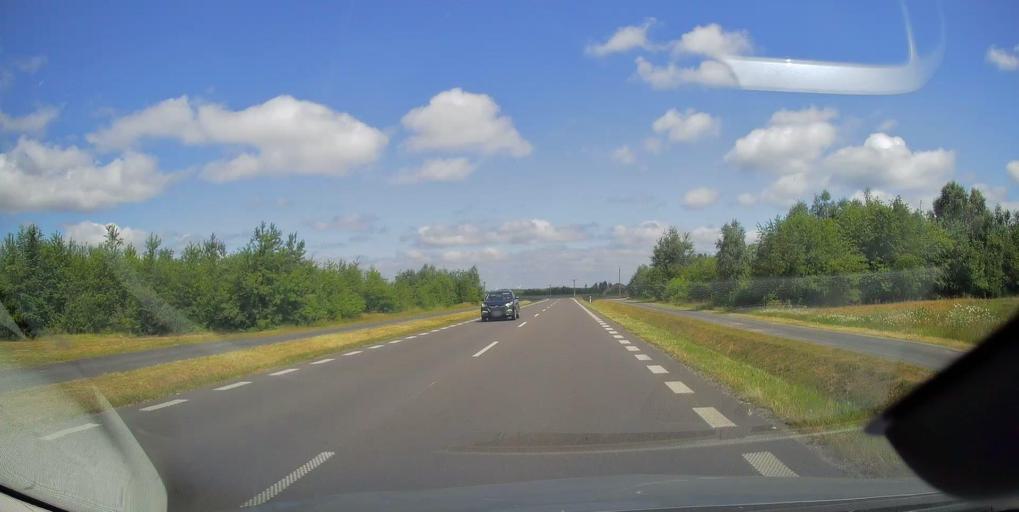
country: PL
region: Subcarpathian Voivodeship
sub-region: Powiat mielecki
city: Mielec
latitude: 50.3353
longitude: 21.4912
